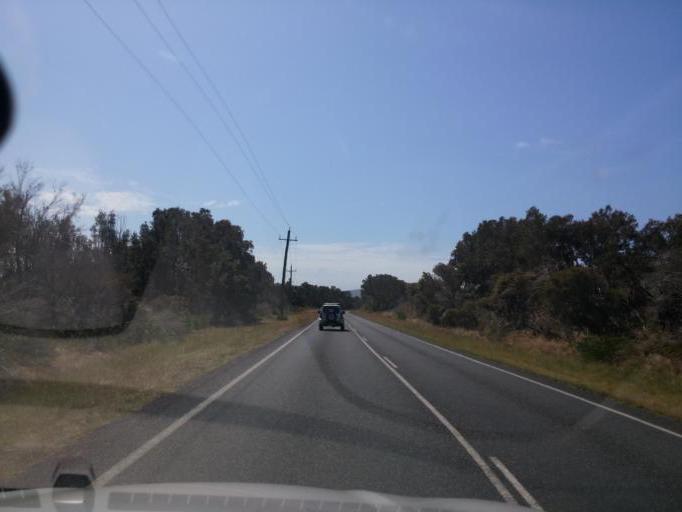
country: AU
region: New South Wales
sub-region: Great Lakes
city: Forster
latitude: -32.2521
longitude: 152.5364
